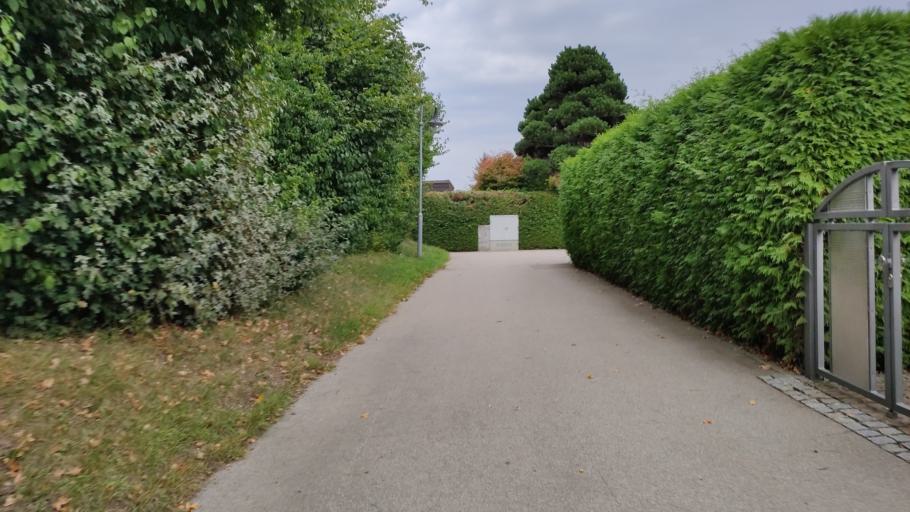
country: DE
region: Bavaria
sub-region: Swabia
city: Konigsbrunn
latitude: 48.2807
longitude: 10.8809
